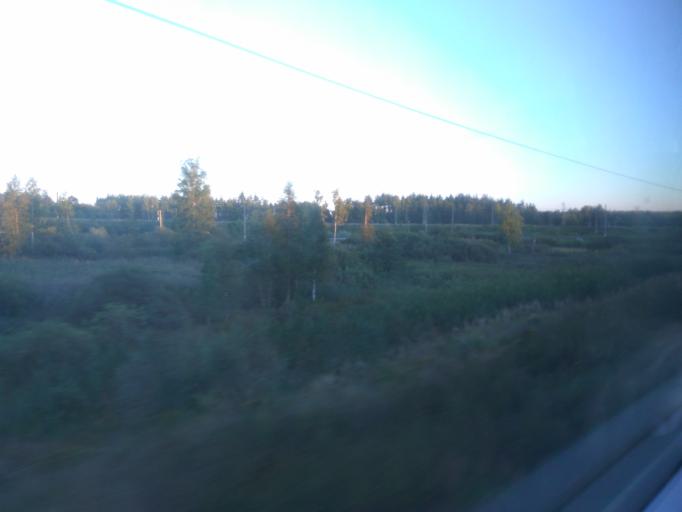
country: RU
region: Moskovskaya
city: Fryazevo
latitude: 55.7377
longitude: 38.4776
